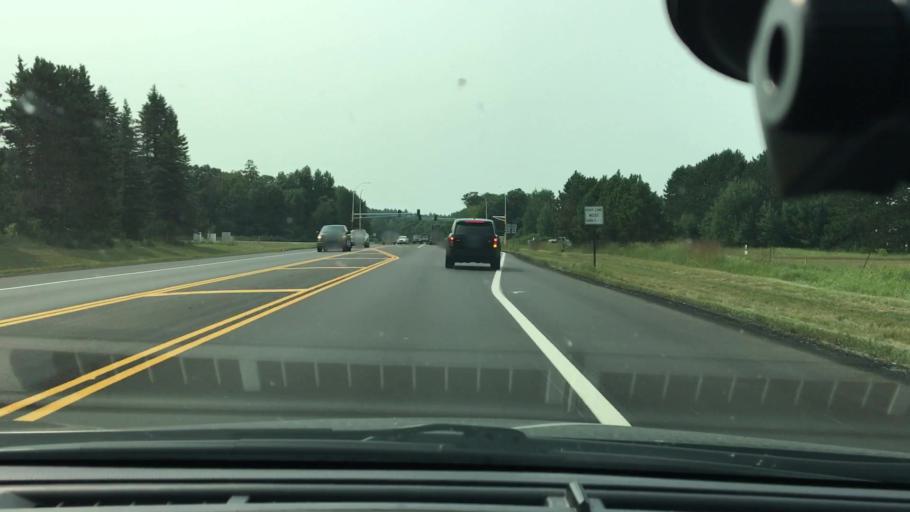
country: US
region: Minnesota
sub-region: Crow Wing County
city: Brainerd
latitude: 46.4004
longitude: -94.1767
